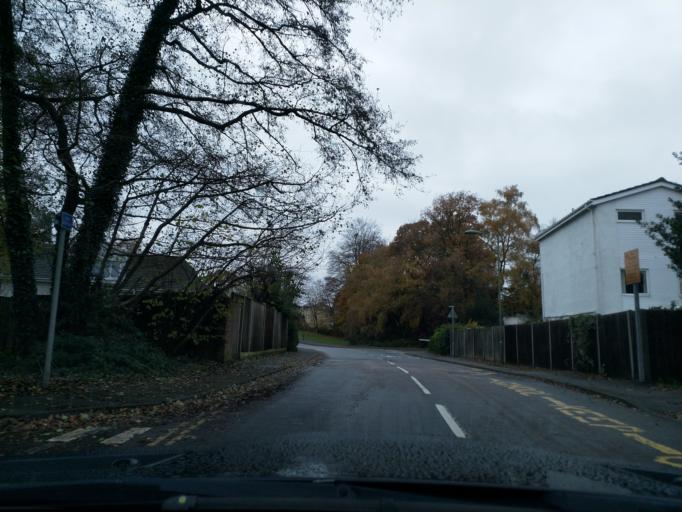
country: GB
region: England
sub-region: Surrey
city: Frimley
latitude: 51.3179
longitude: -0.7302
